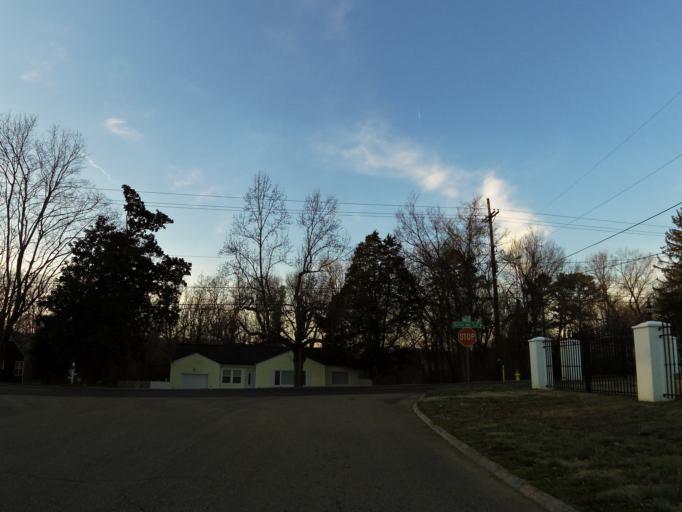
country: US
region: Tennessee
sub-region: Knox County
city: Knoxville
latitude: 36.0202
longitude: -83.8787
